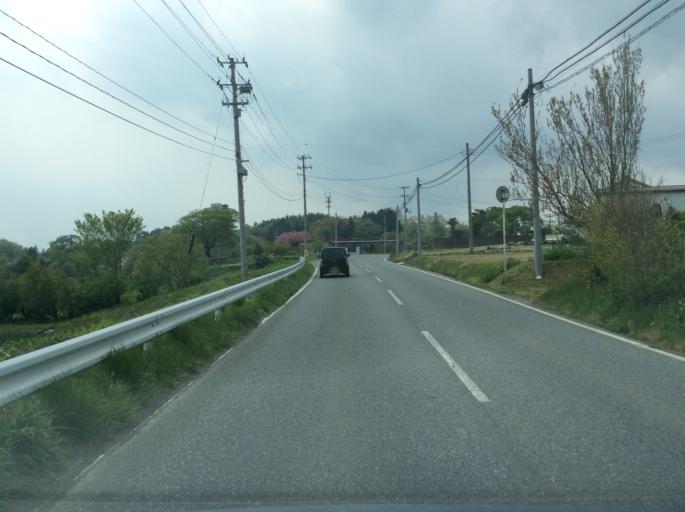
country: JP
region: Fukushima
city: Miharu
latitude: 37.3908
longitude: 140.4457
